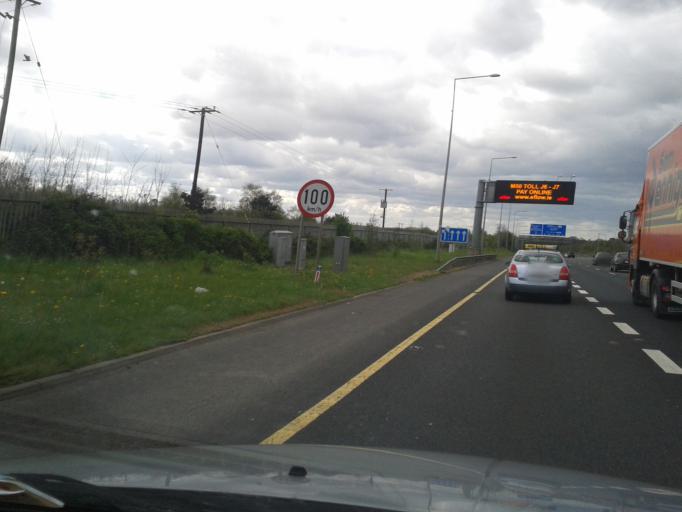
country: IE
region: Leinster
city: Castleknock
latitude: 53.3913
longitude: -6.3466
